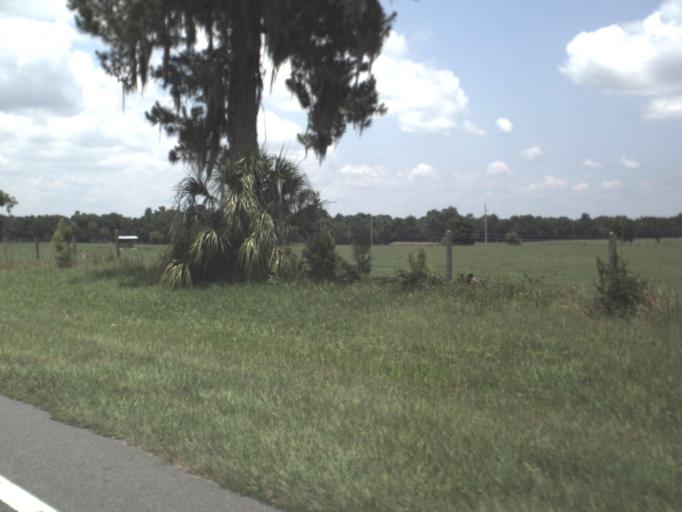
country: US
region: Florida
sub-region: Alachua County
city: Archer
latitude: 29.5087
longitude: -82.4065
